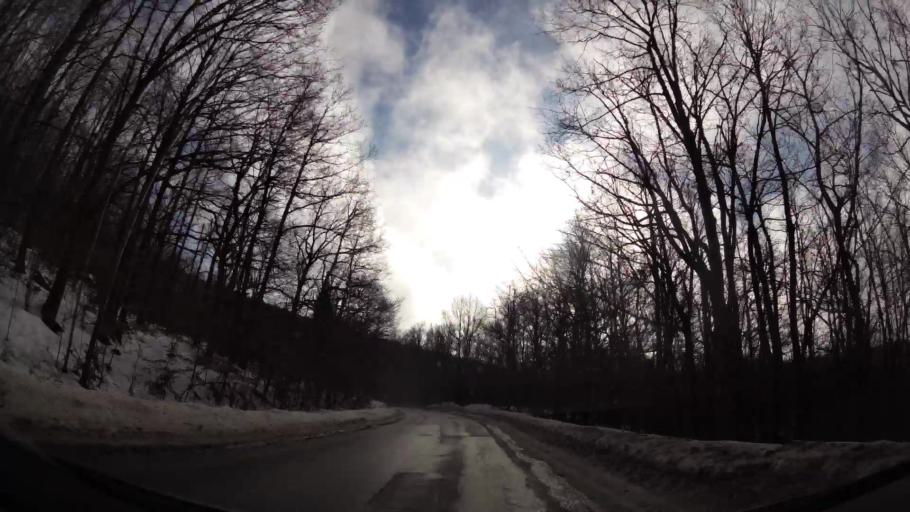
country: BG
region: Sofia-Capital
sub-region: Stolichna Obshtina
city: Sofia
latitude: 42.6325
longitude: 23.2287
